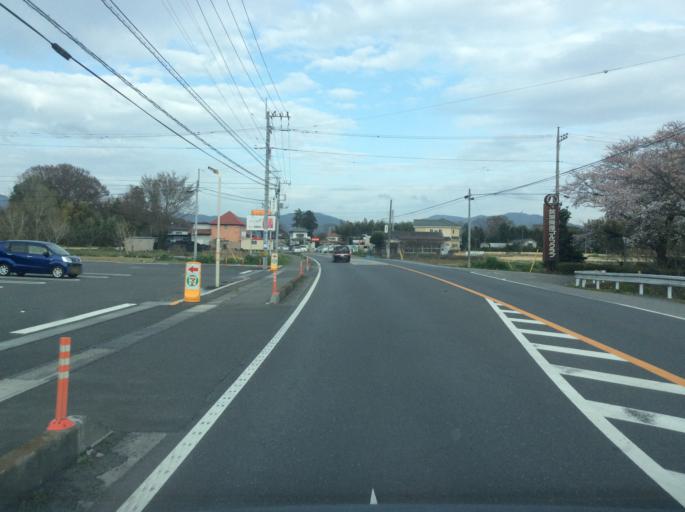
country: JP
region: Ibaraki
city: Tsukuba
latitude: 36.1799
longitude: 140.0496
